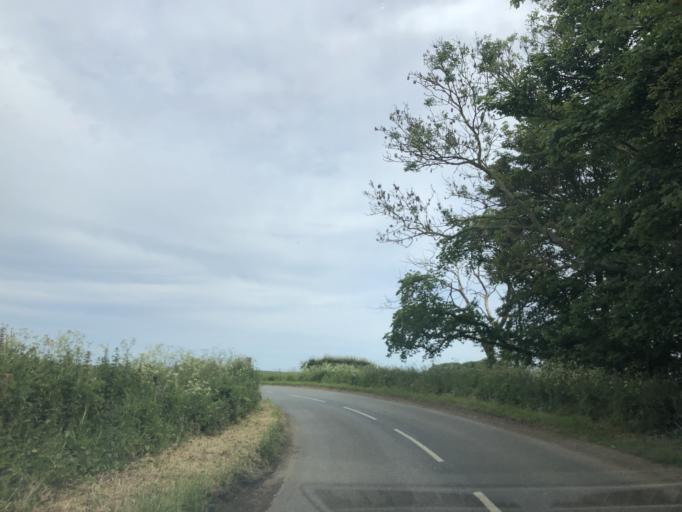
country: GB
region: Scotland
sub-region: Fife
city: Anstruther
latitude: 56.2655
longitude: -2.6578
